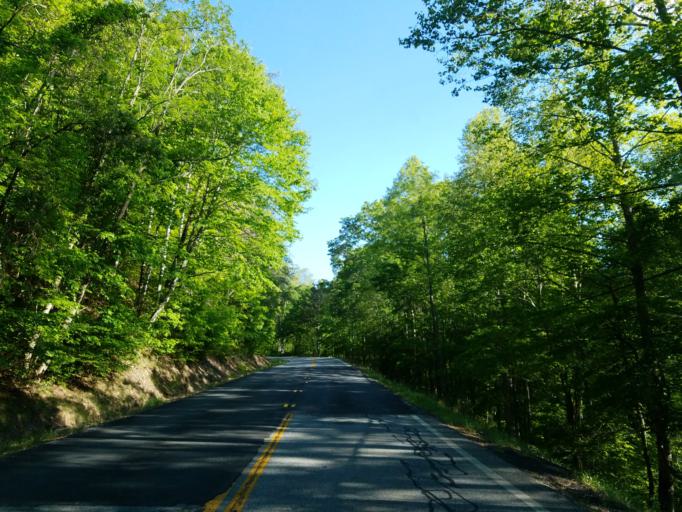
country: US
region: Georgia
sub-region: Fannin County
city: Blue Ridge
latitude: 34.8160
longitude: -84.1880
